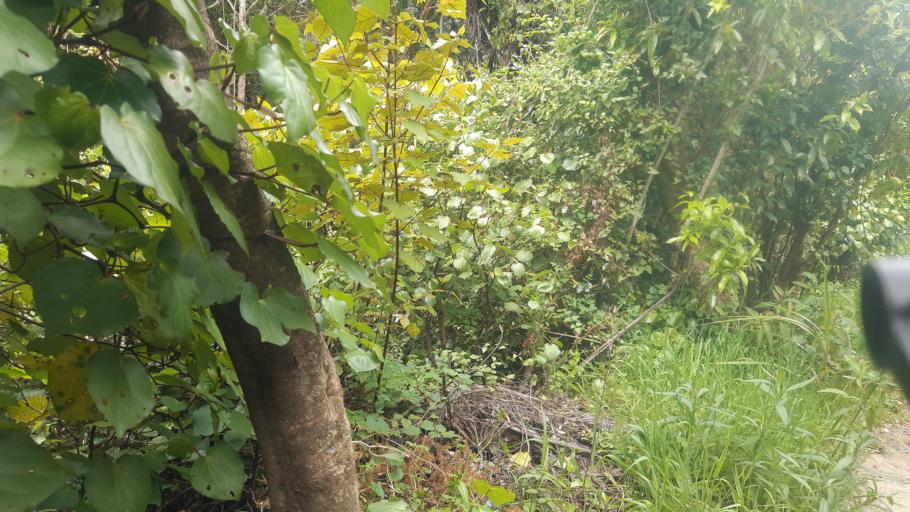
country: NZ
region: Marlborough
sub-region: Marlborough District
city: Picton
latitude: -41.2759
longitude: 173.9932
